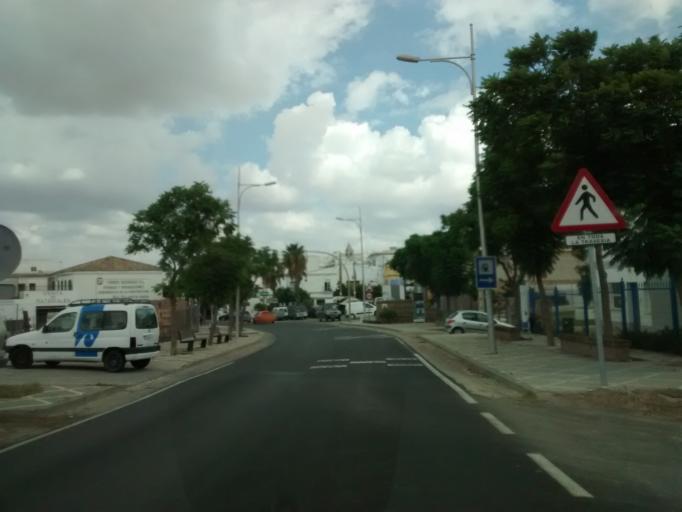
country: ES
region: Andalusia
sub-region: Provincia de Cadiz
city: Paterna de Rivera
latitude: 36.5203
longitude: -5.8677
